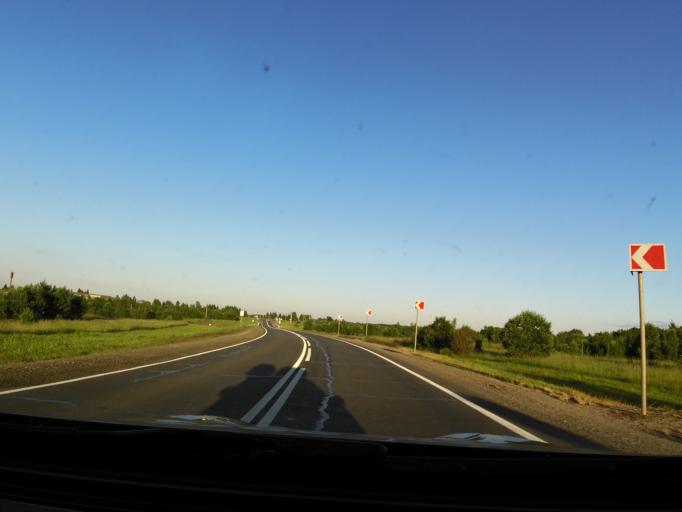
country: RU
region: Vologda
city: Gryazovets
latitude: 58.7979
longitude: 40.2564
